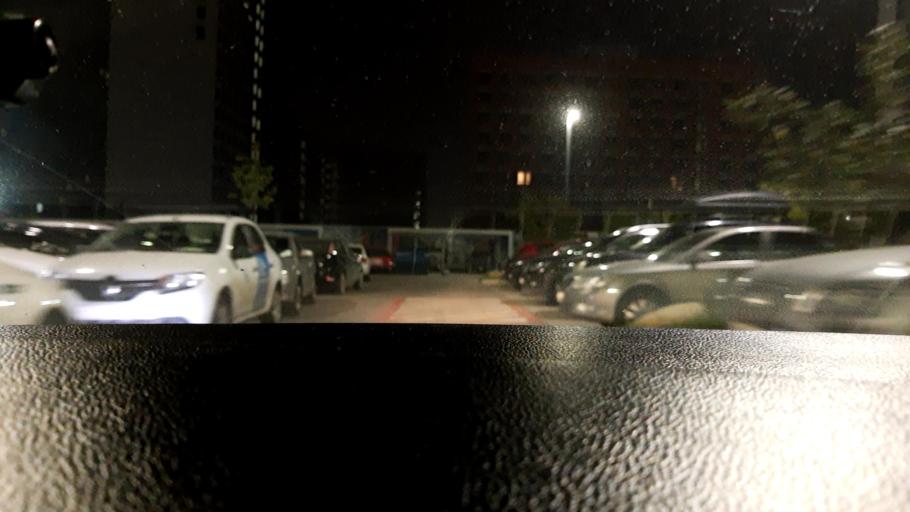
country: RU
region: Moskovskaya
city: Kommunarka
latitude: 55.5441
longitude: 37.4850
